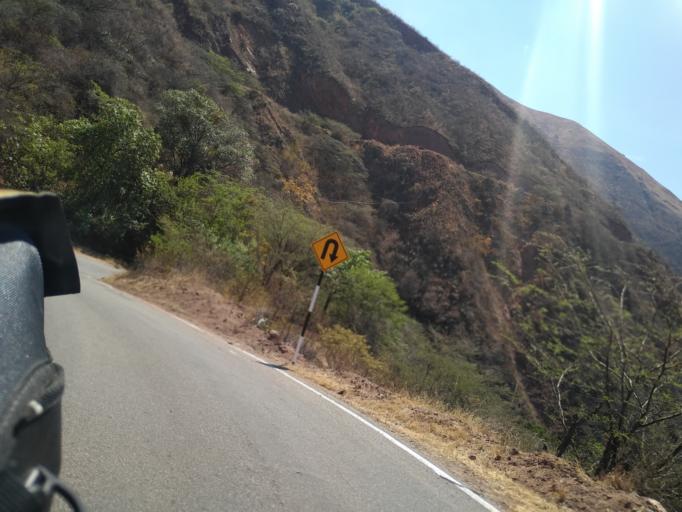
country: PE
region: Amazonas
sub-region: Provincia de Chachapoyas
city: Balsas
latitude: -6.8485
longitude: -77.9675
